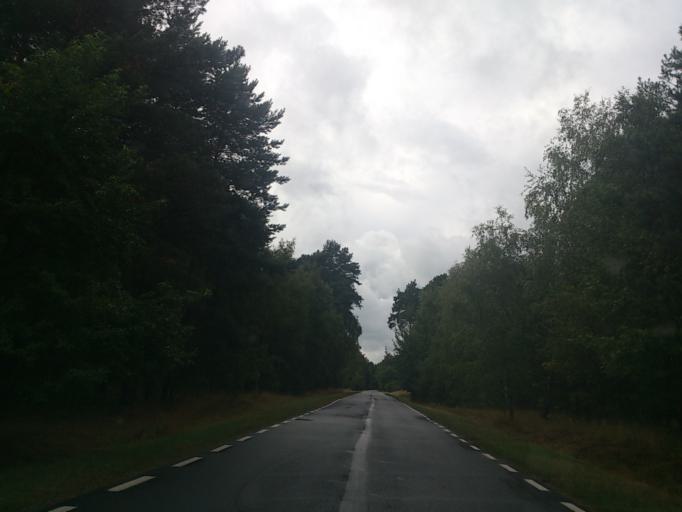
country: PL
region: Greater Poland Voivodeship
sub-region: Powiat gnieznienski
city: Kiszkowo
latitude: 52.5169
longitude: 17.1893
